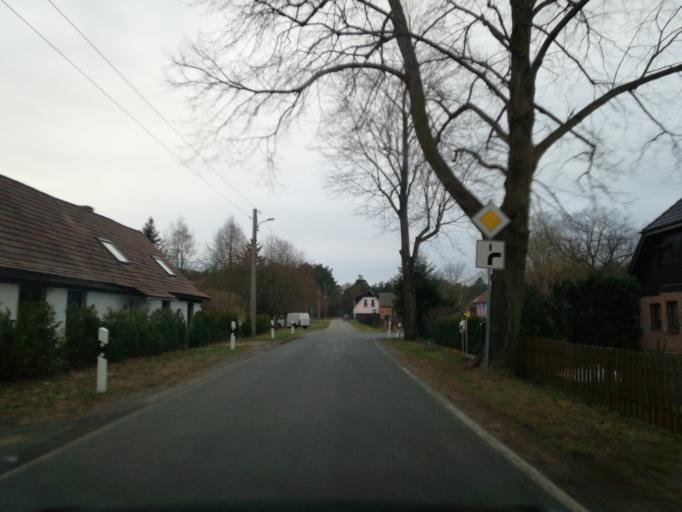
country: DE
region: Brandenburg
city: Vetschau
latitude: 51.7412
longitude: 14.0989
